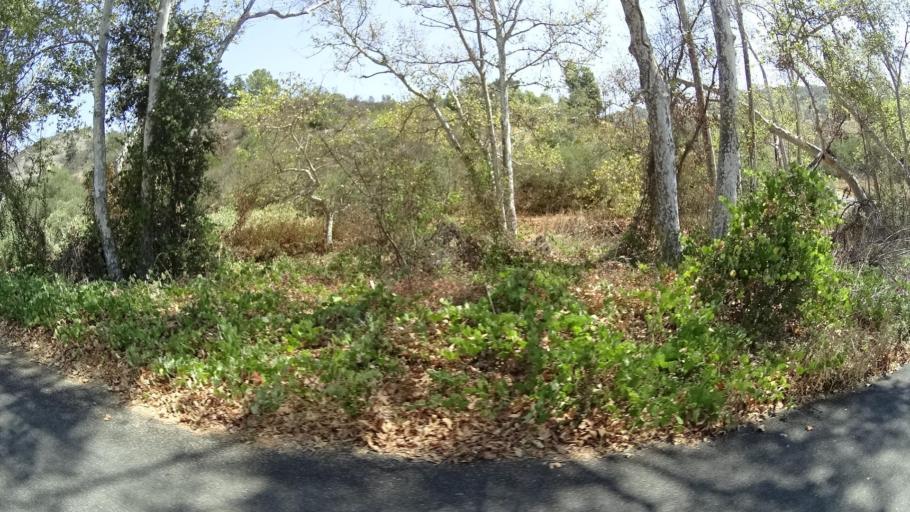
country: US
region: California
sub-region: San Diego County
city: Fallbrook
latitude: 33.4430
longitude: -117.2847
